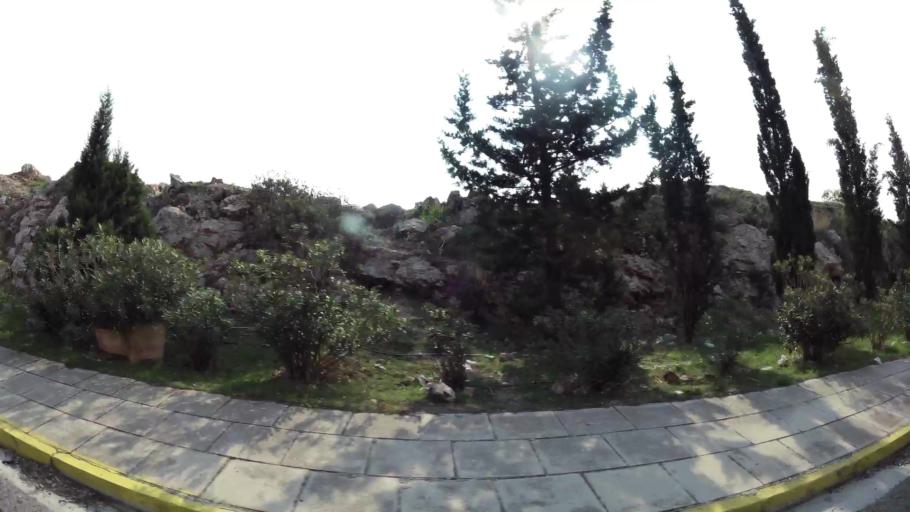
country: GR
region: Attica
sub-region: Nomarchia Athinas
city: Psychiko
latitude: 38.0043
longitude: 23.7633
